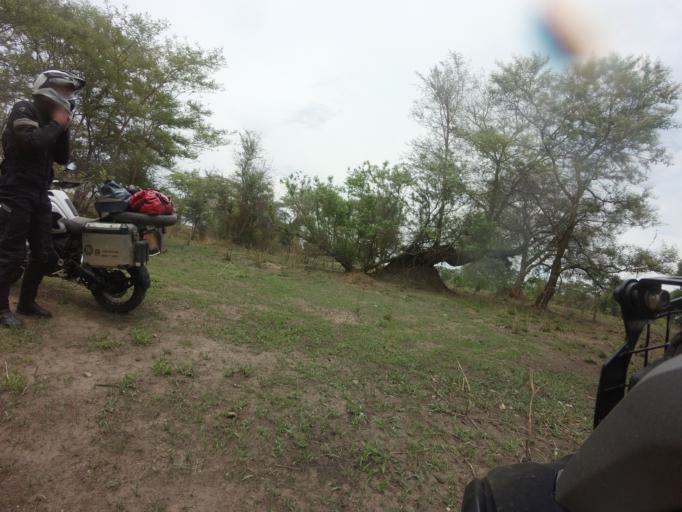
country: BW
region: North West
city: Kasane
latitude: -17.5459
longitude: 25.2086
